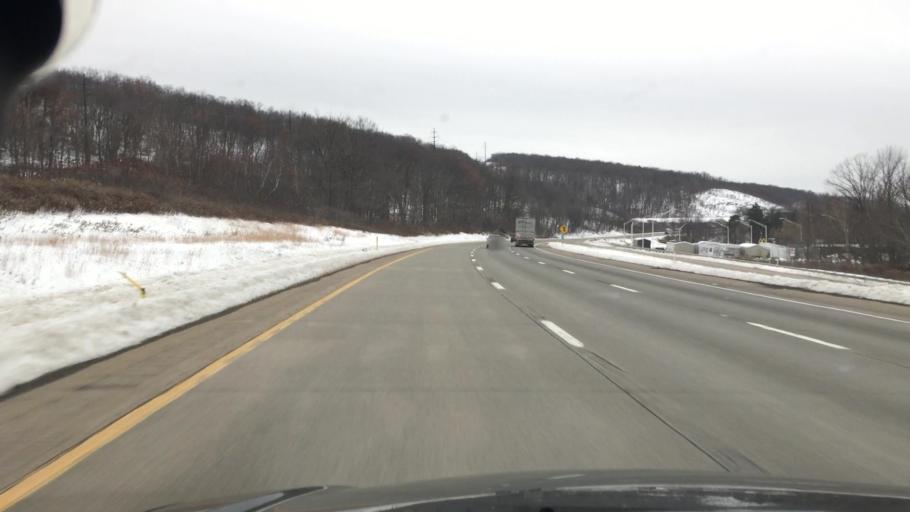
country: US
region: Pennsylvania
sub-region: Luzerne County
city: Freeland
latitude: 41.0814
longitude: -75.9650
